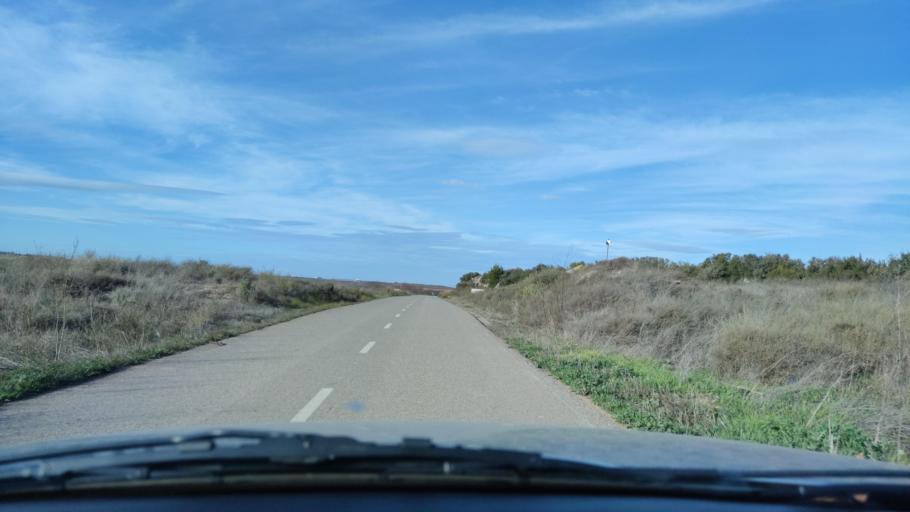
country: ES
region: Catalonia
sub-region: Provincia de Lleida
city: Alcano
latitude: 41.4681
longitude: 0.6458
